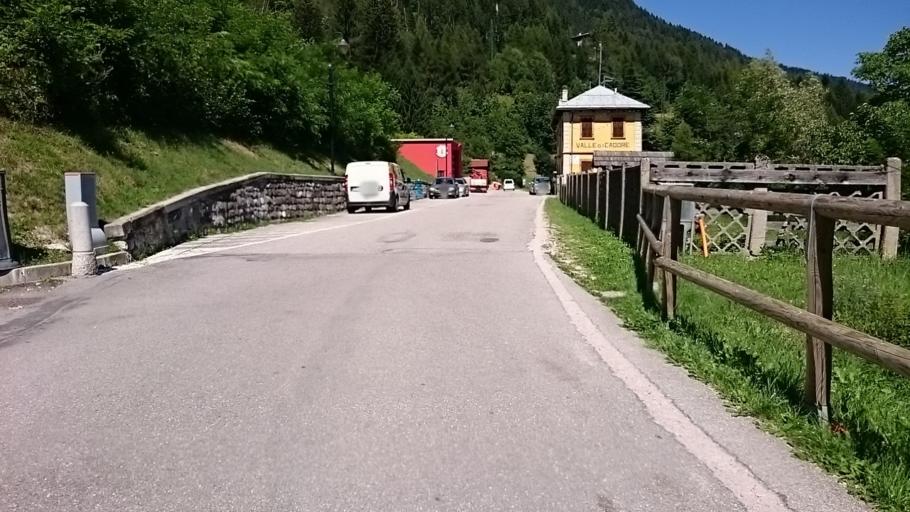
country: IT
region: Veneto
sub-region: Provincia di Belluno
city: Valle di Cadore
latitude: 46.4172
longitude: 12.3267
